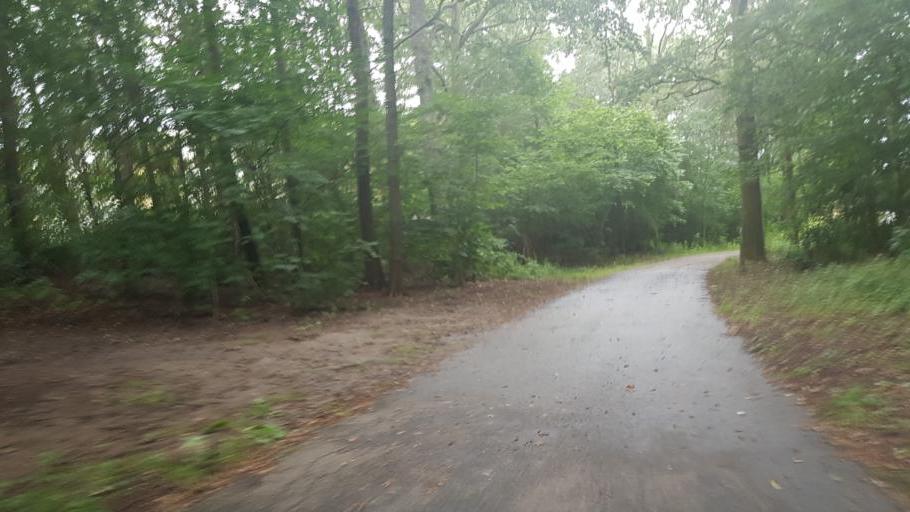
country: SE
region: Vaestra Goetaland
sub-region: Harryda Kommun
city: Molnlycke
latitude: 57.6630
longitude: 12.0984
